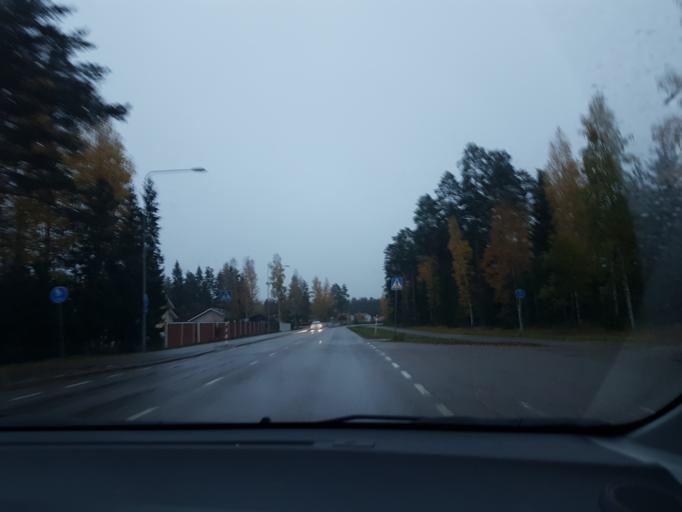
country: FI
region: Uusimaa
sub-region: Helsinki
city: Tuusula
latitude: 60.3994
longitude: 24.9830
